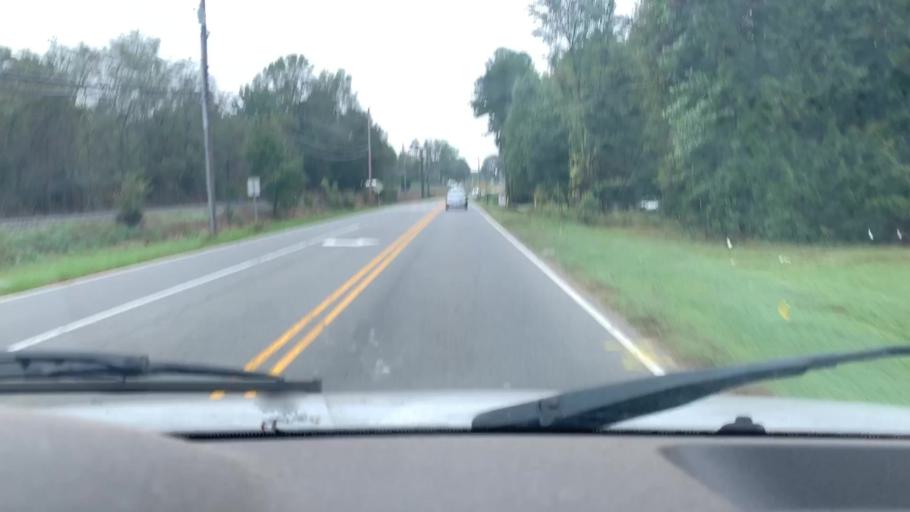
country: US
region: North Carolina
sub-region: Gaston County
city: Davidson
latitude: 35.5358
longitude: -80.8471
